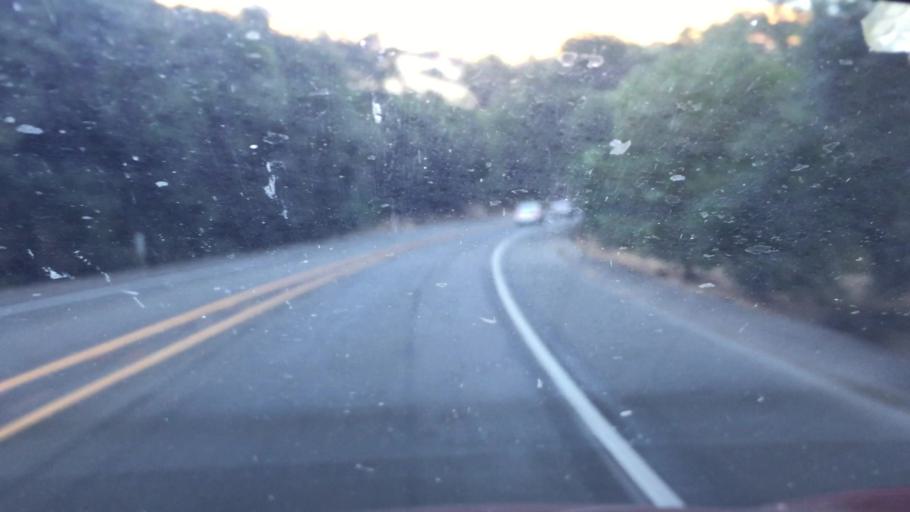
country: US
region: California
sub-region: Alameda County
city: Fremont
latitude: 37.5986
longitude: -121.9263
